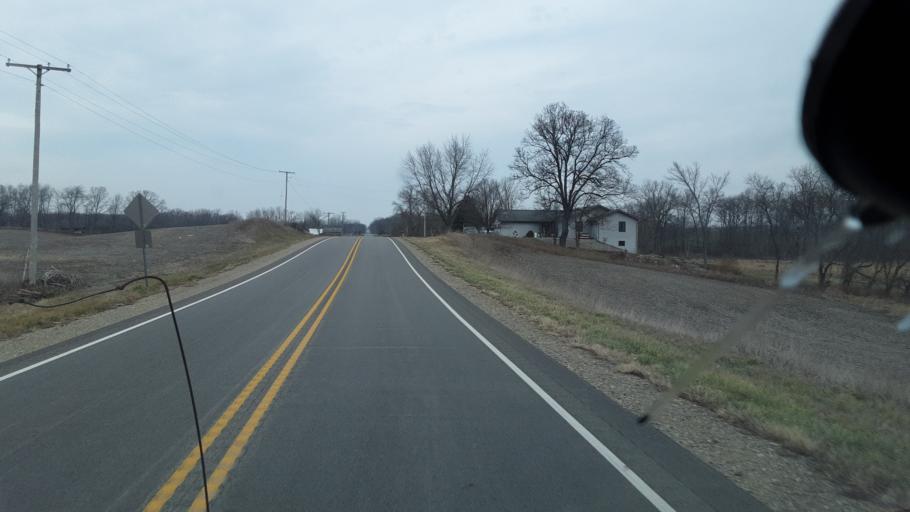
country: US
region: Indiana
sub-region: Noble County
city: Kendallville
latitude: 41.5604
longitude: -85.1683
